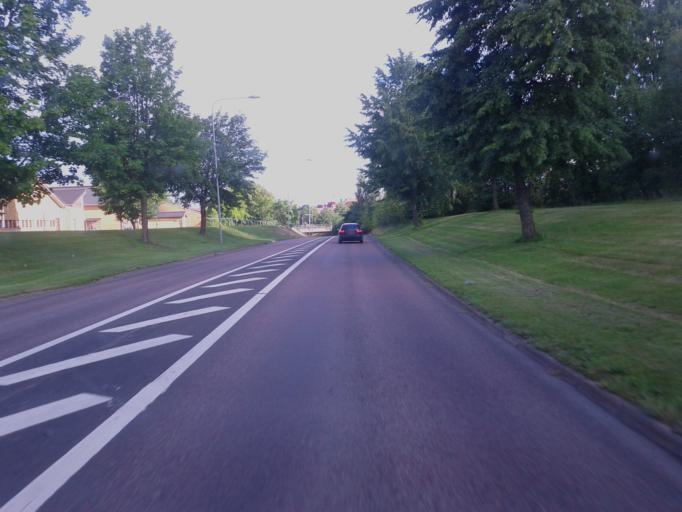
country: SE
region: Dalarna
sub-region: Borlange Kommun
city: Borlaenge
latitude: 60.4920
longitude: 15.4333
